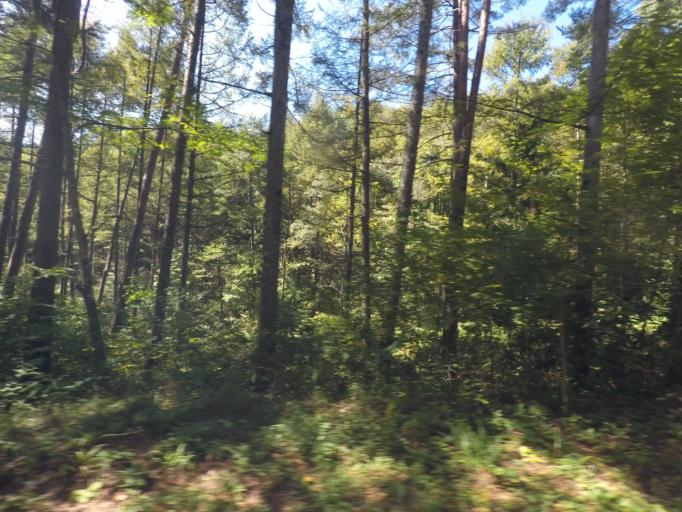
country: JP
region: Nagano
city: Shiojiri
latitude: 35.9948
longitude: 137.7345
